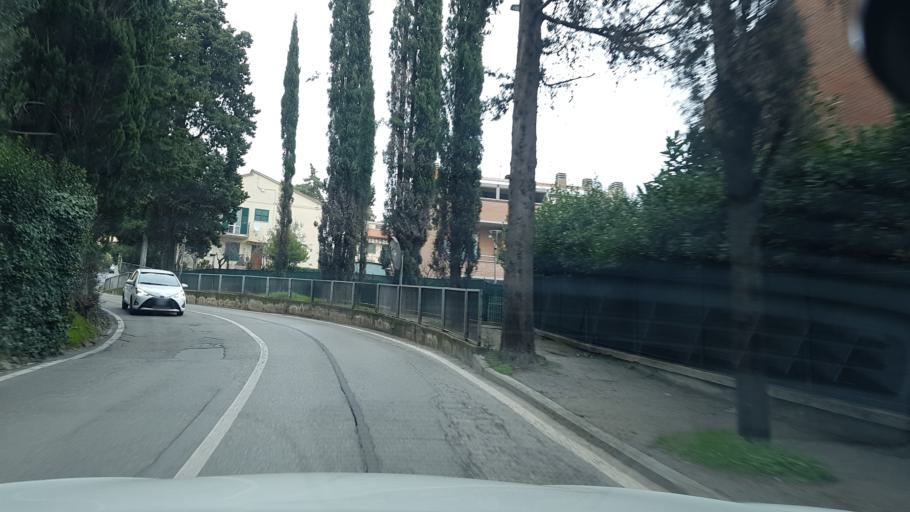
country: IT
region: Umbria
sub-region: Provincia di Perugia
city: Perugia
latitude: 43.1161
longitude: 12.3649
